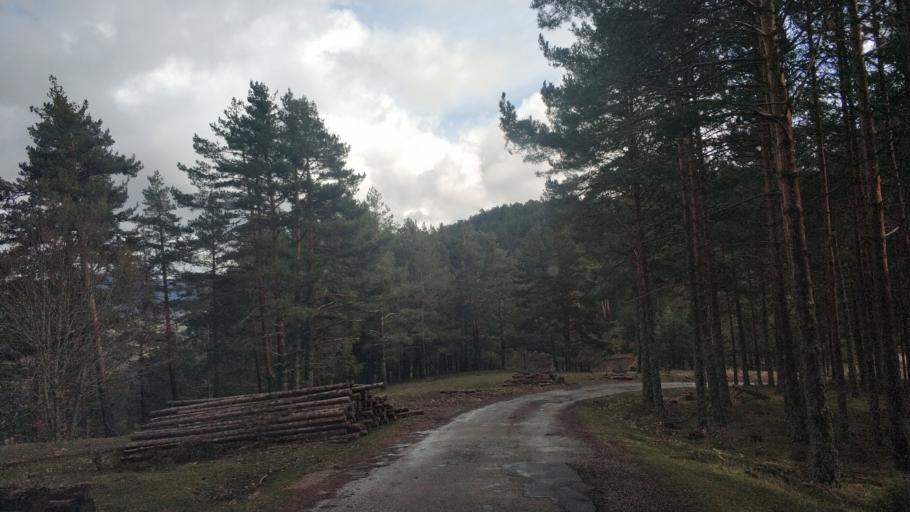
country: ES
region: Castille and Leon
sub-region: Provincia de Burgos
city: Neila
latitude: 42.0432
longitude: -3.0119
